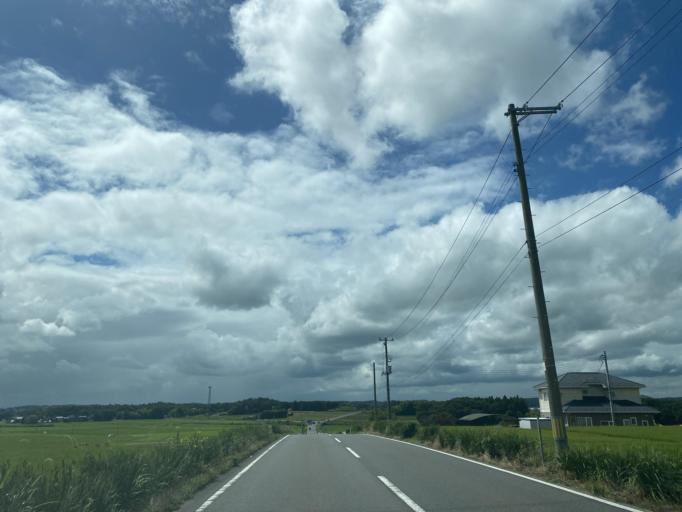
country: JP
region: Fukushima
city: Koriyama
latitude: 37.3734
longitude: 140.2940
